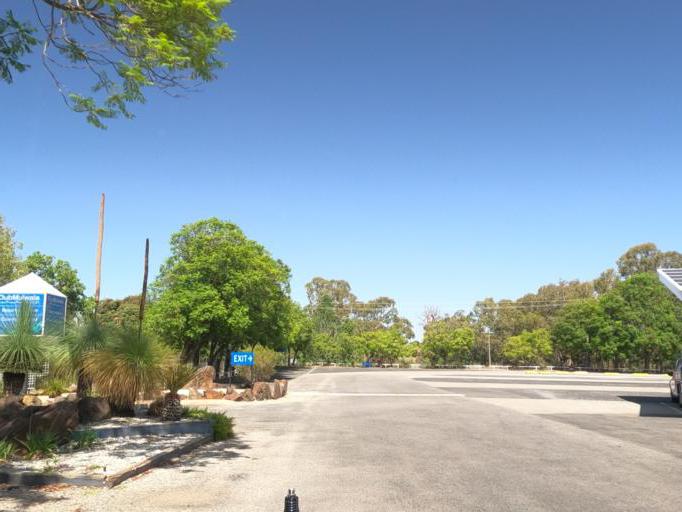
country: AU
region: New South Wales
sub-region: Corowa Shire
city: Mulwala
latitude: -36.0038
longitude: 146.0003
